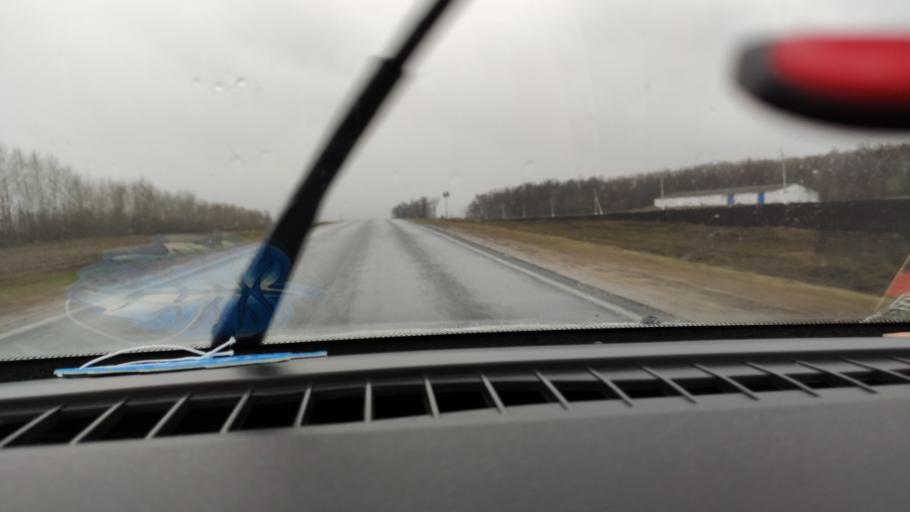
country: RU
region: Tatarstan
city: Cheremshan
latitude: 54.7414
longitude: 51.3552
